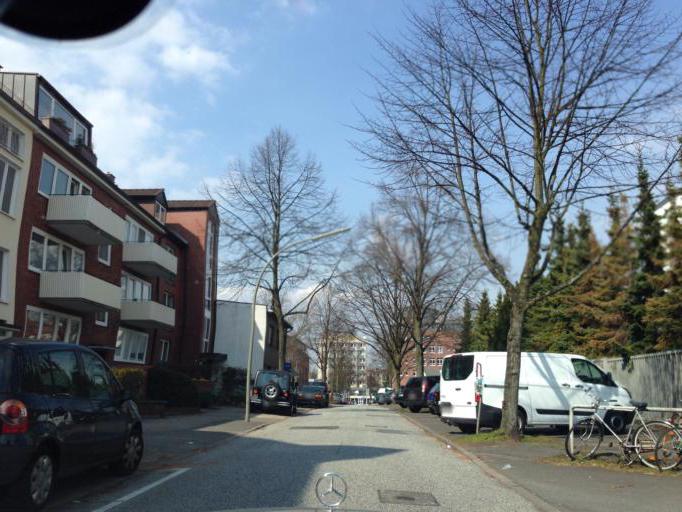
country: DE
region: Hamburg
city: Marienthal
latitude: 53.5738
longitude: 10.0800
